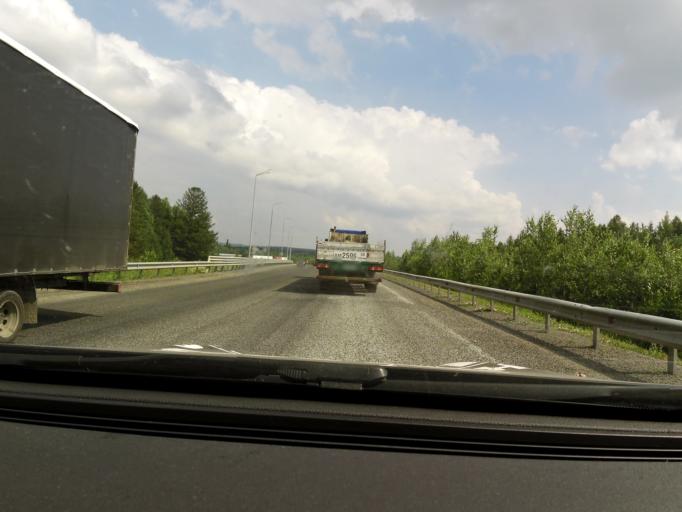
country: RU
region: Sverdlovsk
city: Ufimskiy
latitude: 56.7634
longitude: 58.1440
